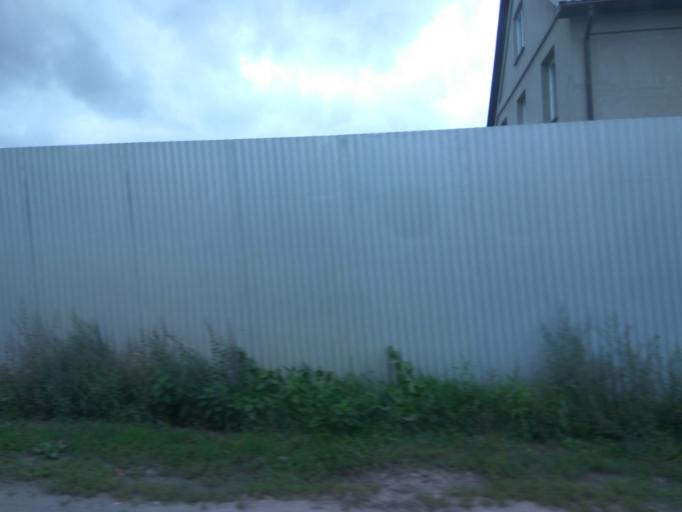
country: RU
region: Moskovskaya
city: Malyshevo
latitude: 55.5009
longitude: 38.3414
